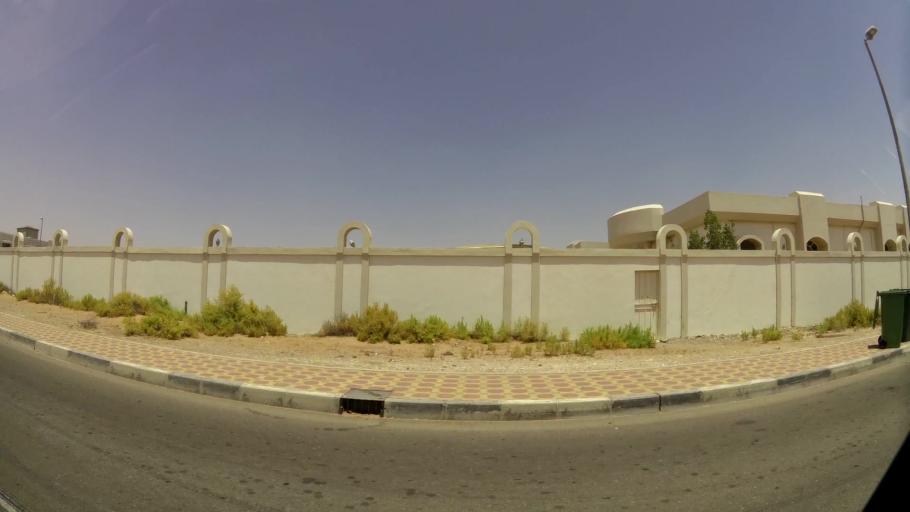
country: OM
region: Al Buraimi
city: Al Buraymi
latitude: 24.2665
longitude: 55.7063
